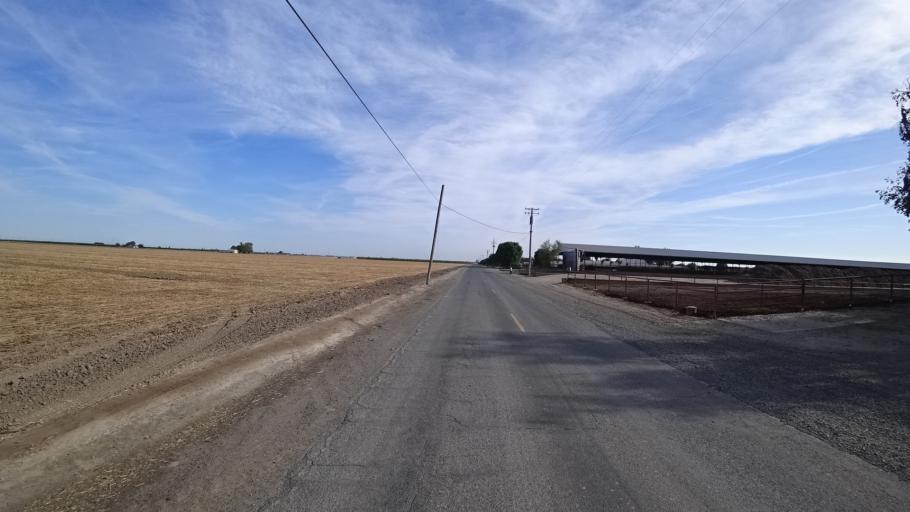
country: US
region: California
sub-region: Kings County
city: Hanford
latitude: 36.3808
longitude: -119.5470
